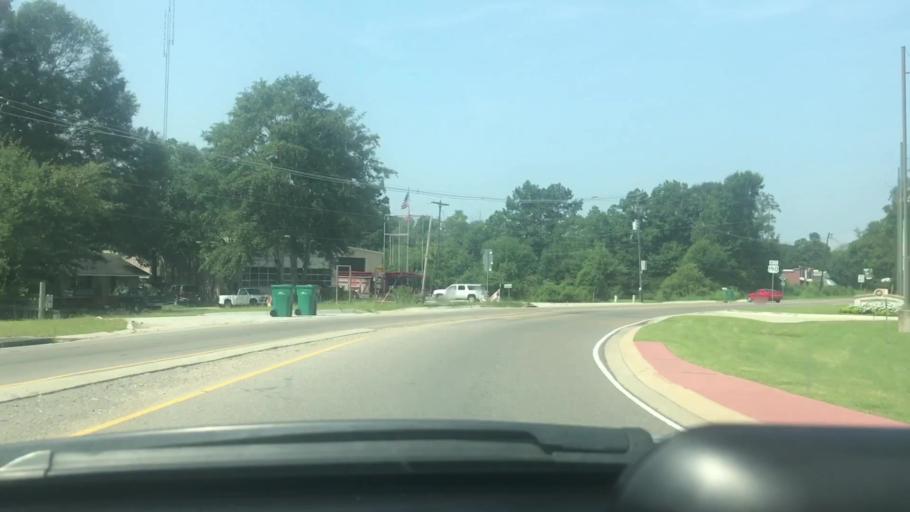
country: US
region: Louisiana
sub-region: Livingston Parish
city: Denham Springs
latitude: 30.4833
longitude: -90.9270
